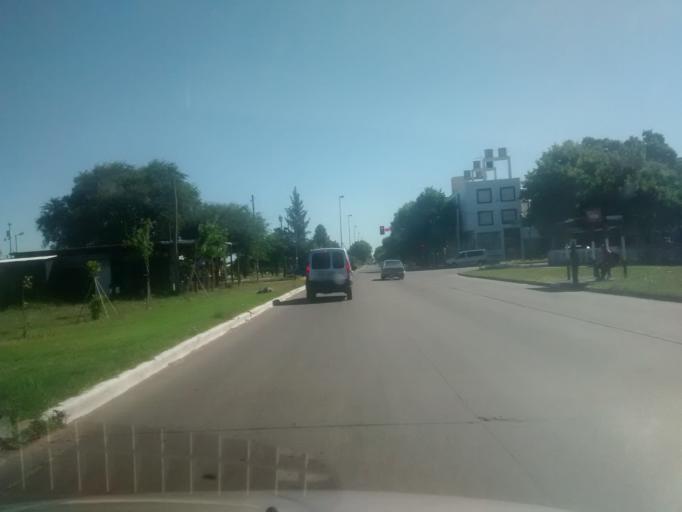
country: AR
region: Buenos Aires
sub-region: Partido de La Plata
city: La Plata
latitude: -34.9249
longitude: -57.9213
